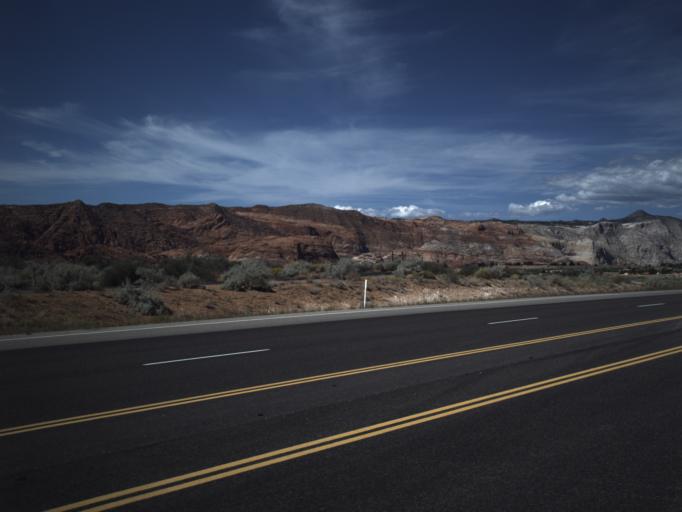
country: US
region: Utah
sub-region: Washington County
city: Ivins
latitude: 37.1905
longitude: -113.6207
